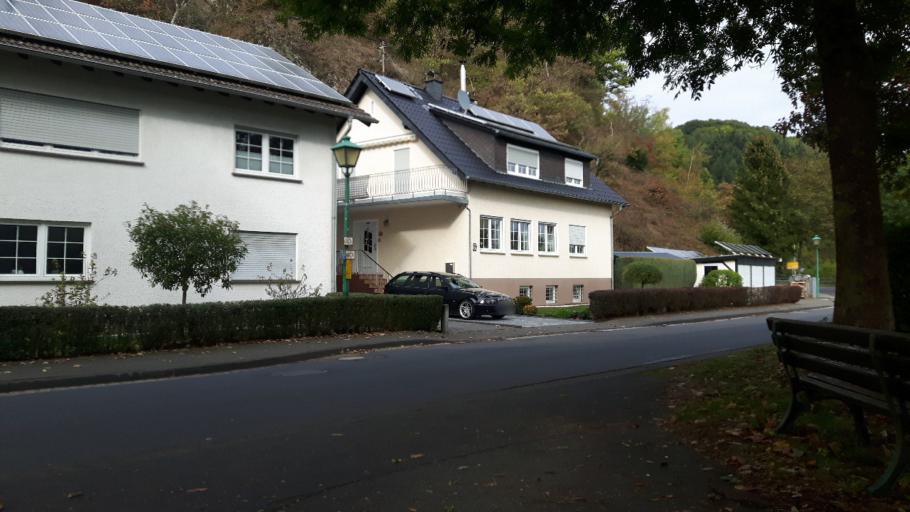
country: DE
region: North Rhine-Westphalia
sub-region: Regierungsbezirk Koln
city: Eitorf
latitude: 50.7788
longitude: 7.4310
